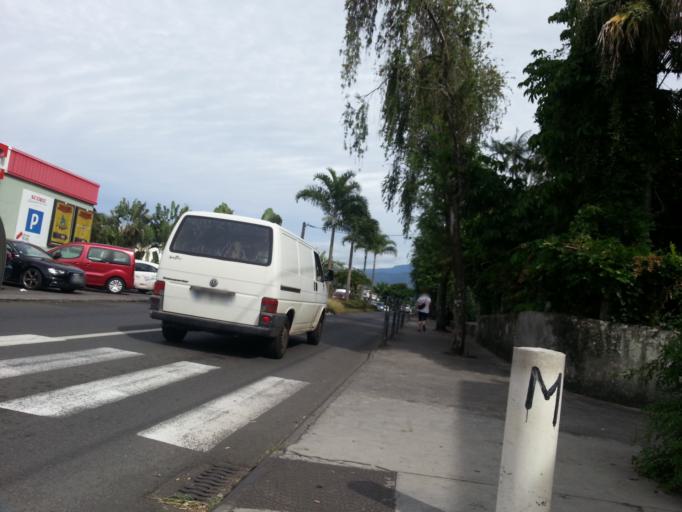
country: RE
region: Reunion
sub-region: Reunion
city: Le Tampon
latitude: -21.2613
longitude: 55.5049
